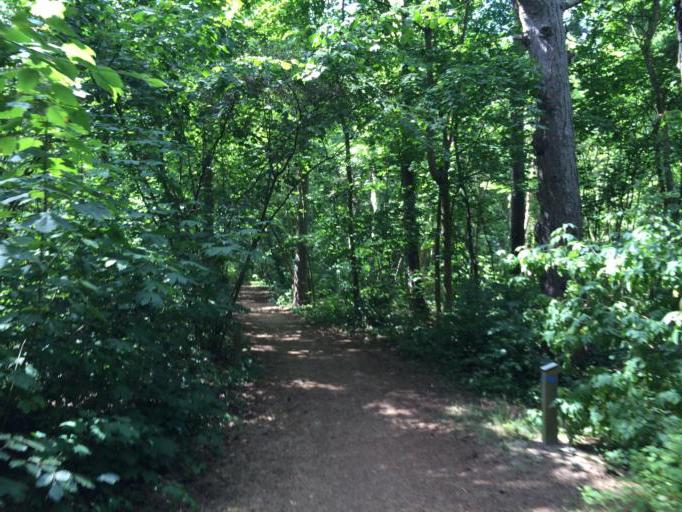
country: SE
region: Skane
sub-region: Vellinge Kommun
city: Skanor med Falsterbo
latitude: 55.3921
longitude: 12.8405
